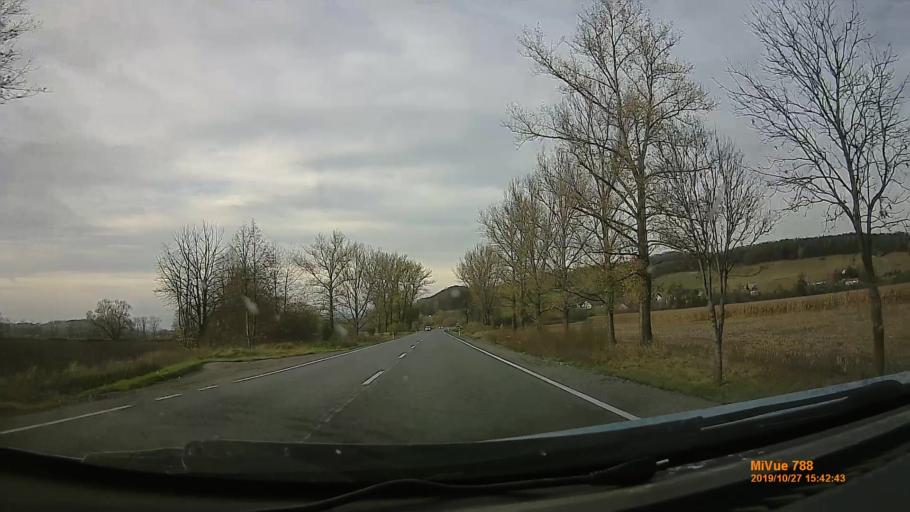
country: PL
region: Lower Silesian Voivodeship
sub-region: Powiat klodzki
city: Klodzko
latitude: 50.4623
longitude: 16.6248
